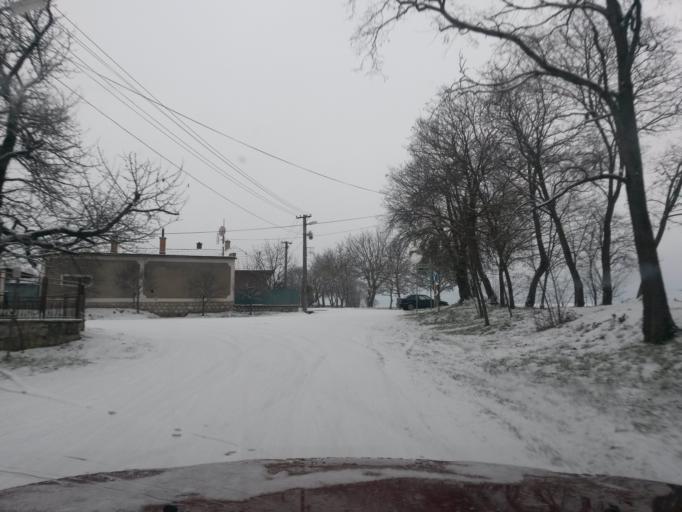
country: SK
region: Kosicky
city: Moldava nad Bodvou
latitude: 48.5996
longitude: 21.0222
